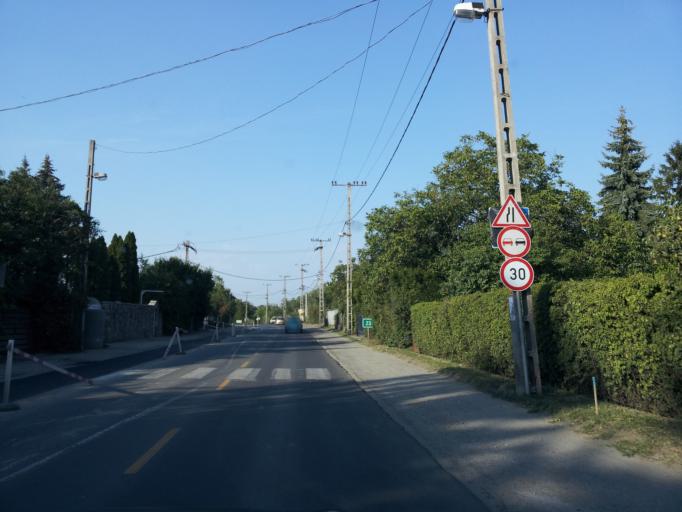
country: HU
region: Pest
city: Szentendre
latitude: 47.6871
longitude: 19.0844
